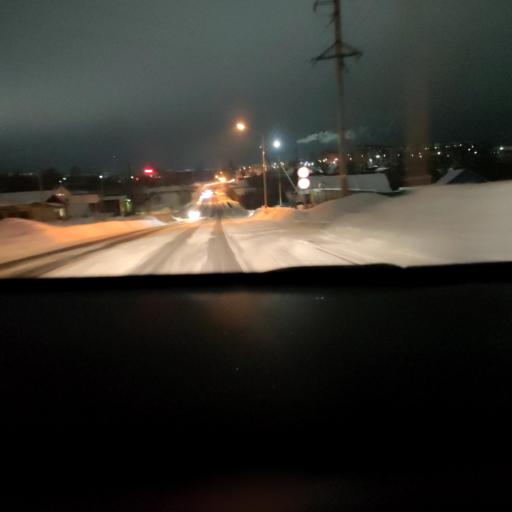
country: RU
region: Tatarstan
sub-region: Chistopol'skiy Rayon
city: Chistopol'
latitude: 55.3584
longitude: 50.6163
